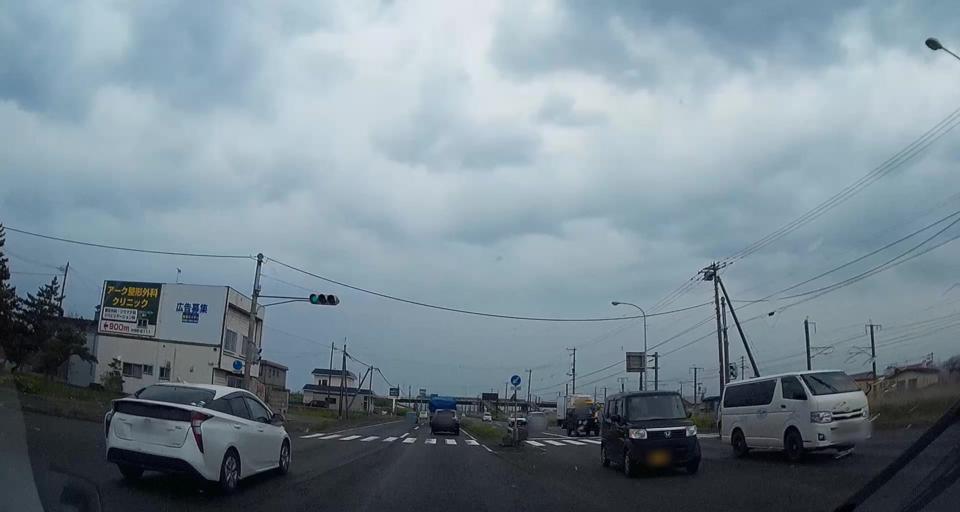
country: JP
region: Hokkaido
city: Tomakomai
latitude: 42.6116
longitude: 141.5149
